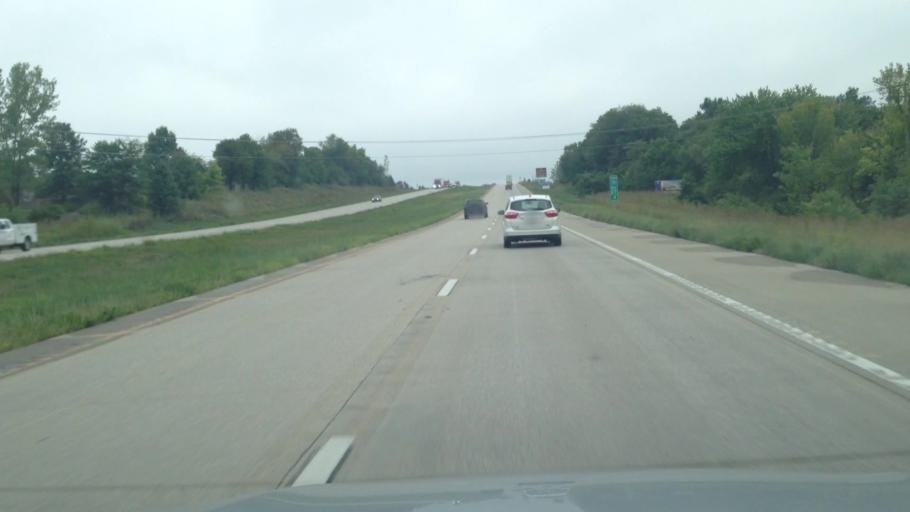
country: US
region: Missouri
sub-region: Clay County
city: Kearney
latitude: 39.3848
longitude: -94.3634
